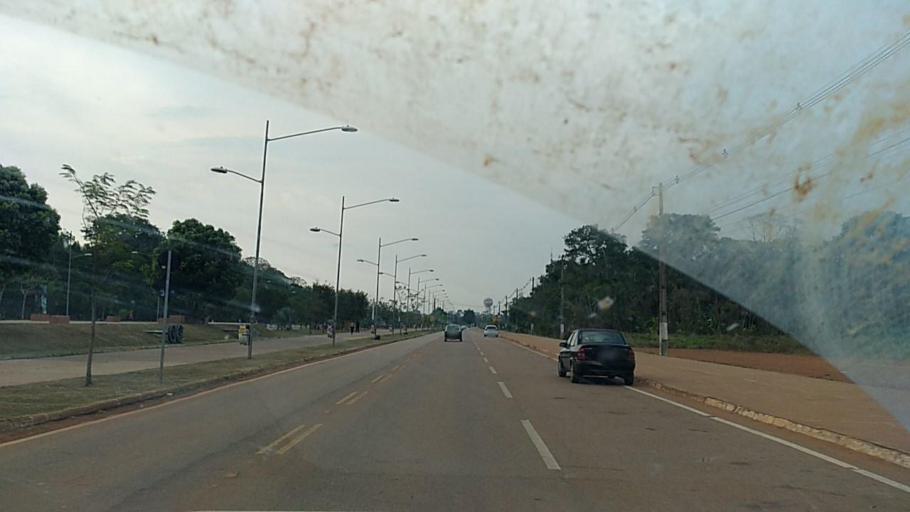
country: BR
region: Rondonia
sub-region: Porto Velho
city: Porto Velho
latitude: -8.7215
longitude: -63.8940
